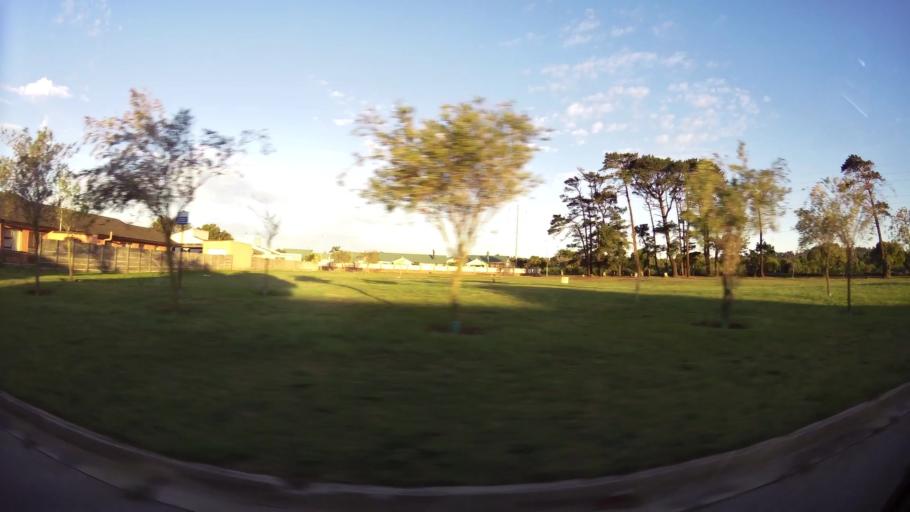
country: ZA
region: Eastern Cape
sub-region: Nelson Mandela Bay Metropolitan Municipality
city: Port Elizabeth
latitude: -33.9734
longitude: 25.5183
